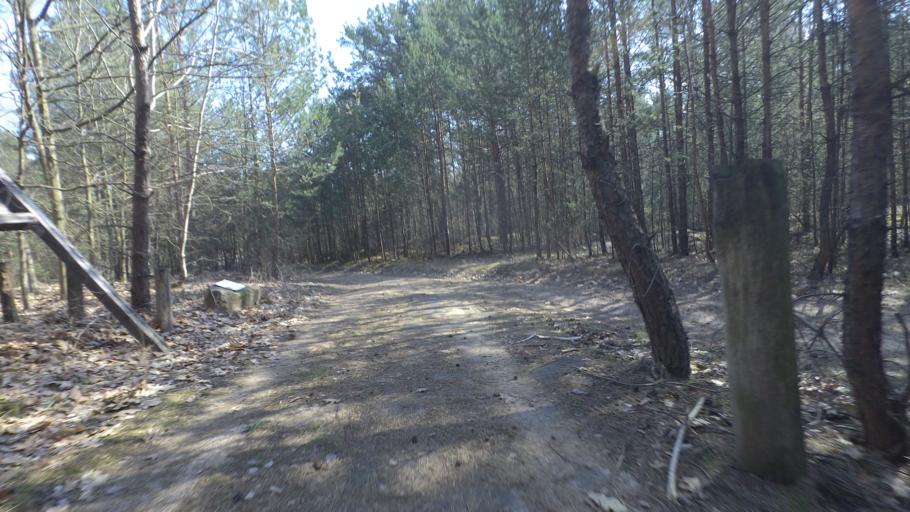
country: DE
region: Brandenburg
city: Mittenwalde
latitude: 52.1819
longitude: 13.5524
